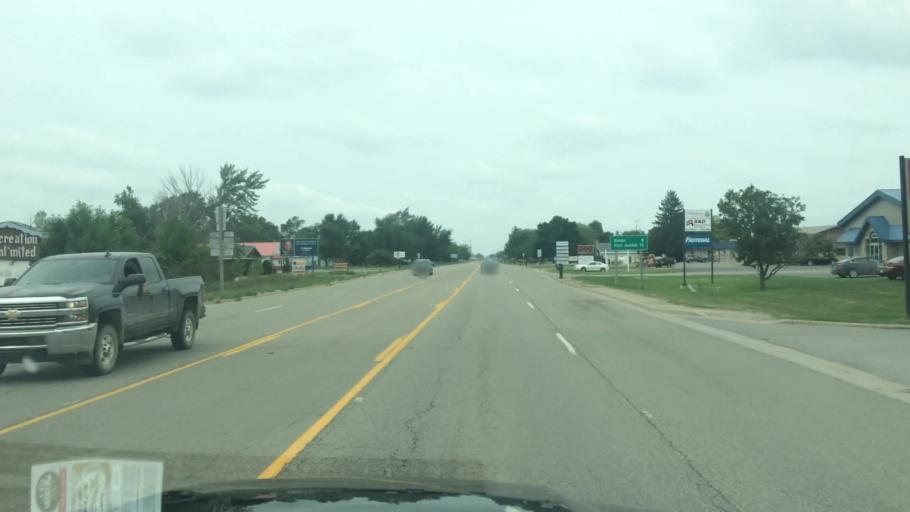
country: US
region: Michigan
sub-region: Huron County
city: Bad Axe
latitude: 43.8255
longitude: -83.0011
